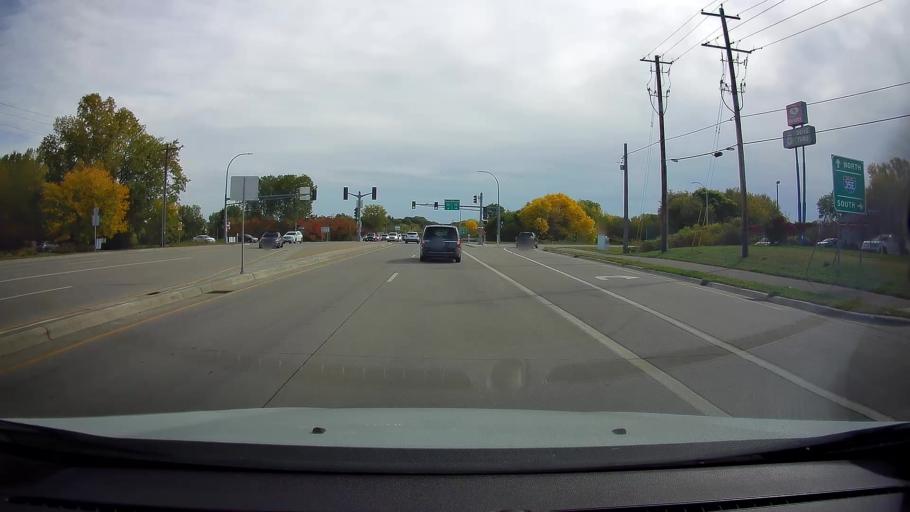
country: US
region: Minnesota
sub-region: Ramsey County
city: Vadnais Heights
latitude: 45.0792
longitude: -93.0552
